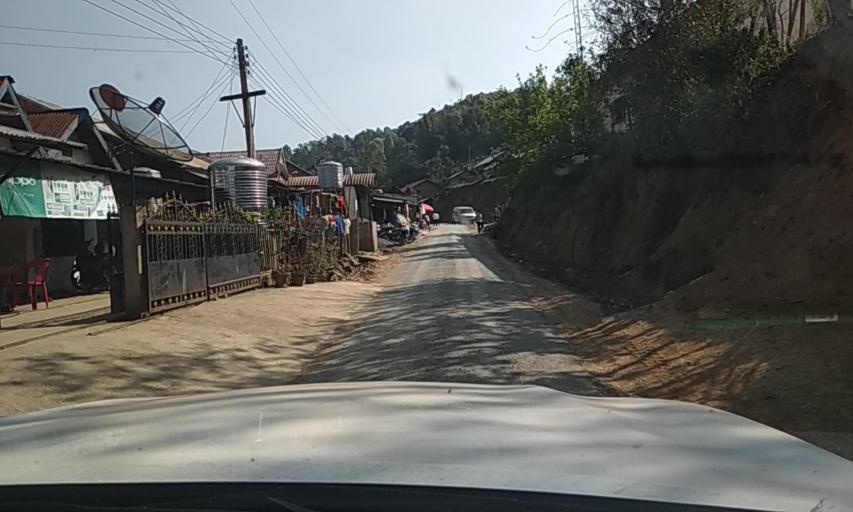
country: LA
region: Phongsali
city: Phongsali
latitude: 21.6641
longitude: 102.0893
